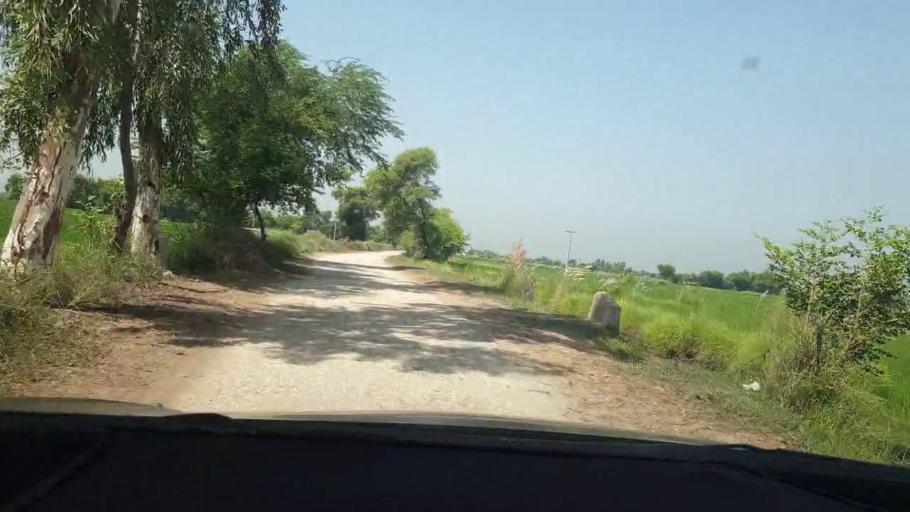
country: PK
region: Sindh
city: Kambar
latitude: 27.6110
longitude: 68.0622
